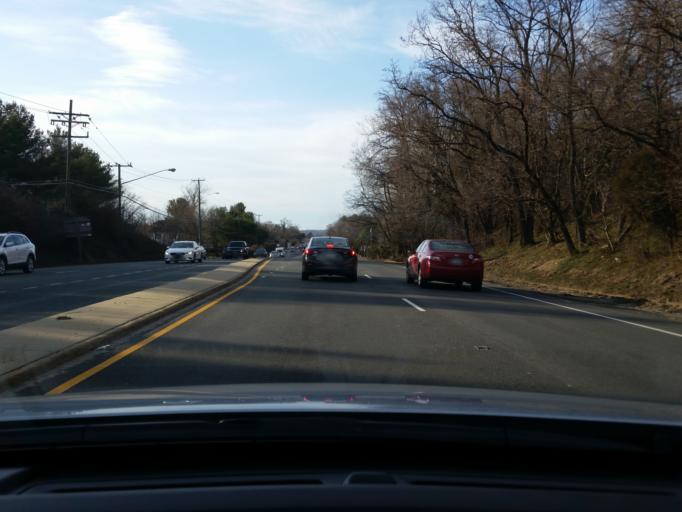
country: US
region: Virginia
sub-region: Fairfax County
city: Wolf Trap
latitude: 38.9520
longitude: -77.2655
